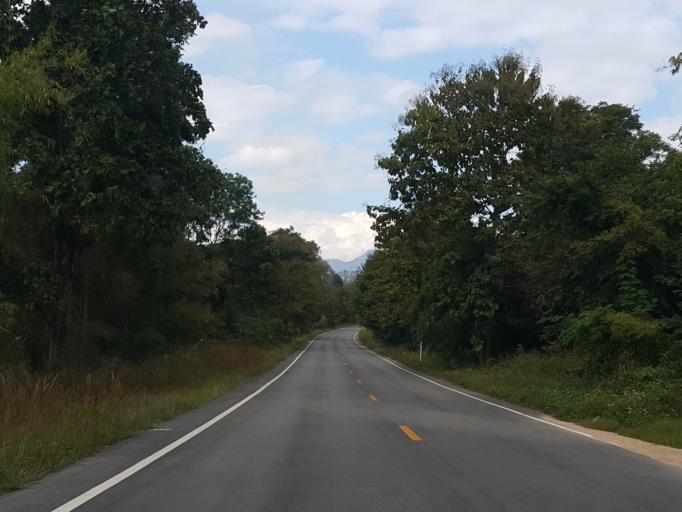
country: TH
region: Lampang
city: Chae Hom
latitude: 18.6116
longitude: 99.4829
